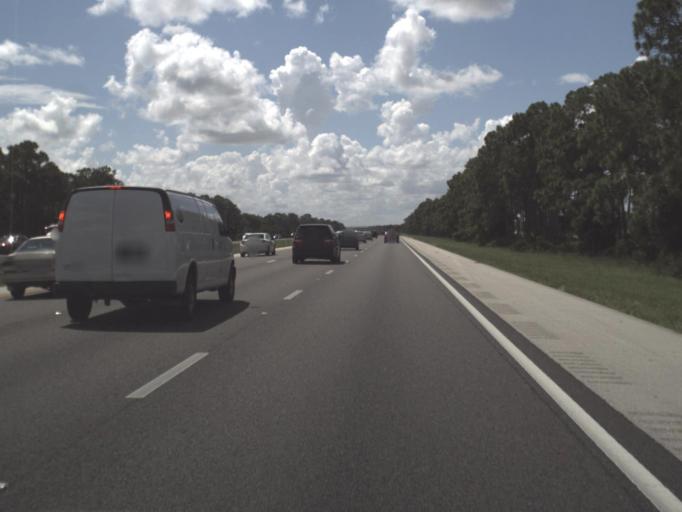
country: US
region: Florida
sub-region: Lee County
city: Three Oaks
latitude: 26.4645
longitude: -81.7888
